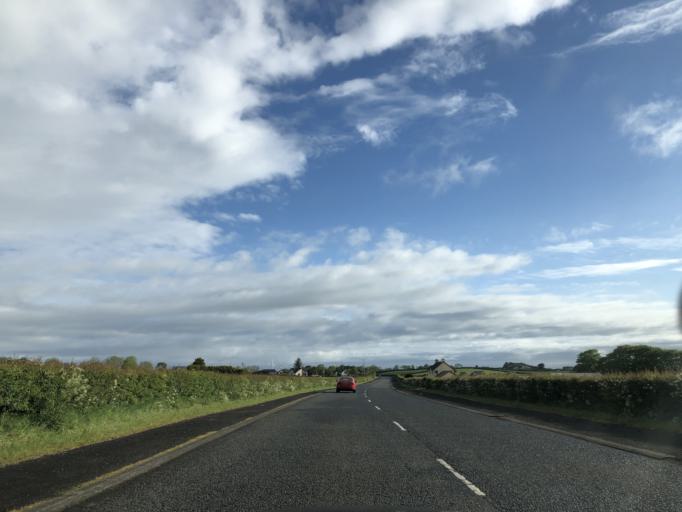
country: GB
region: Northern Ireland
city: Bushmills
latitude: 55.1605
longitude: -6.5753
